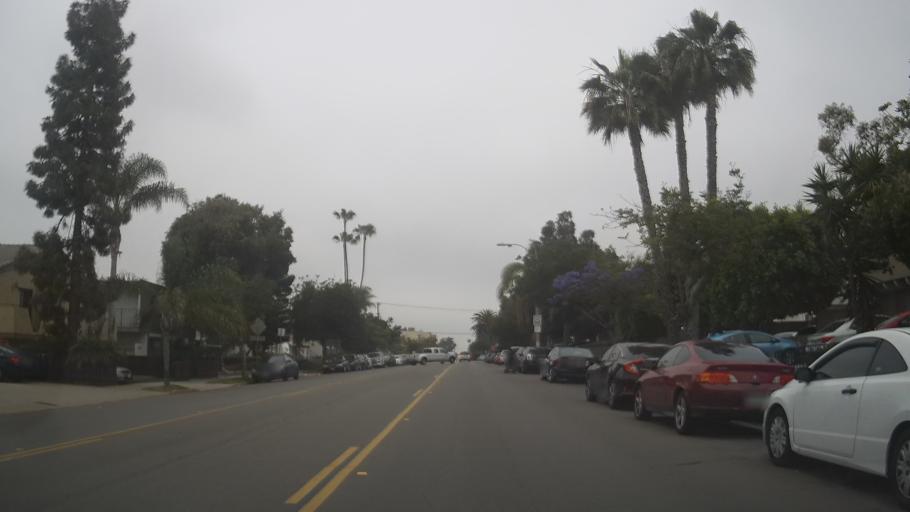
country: US
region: California
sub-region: San Diego County
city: San Diego
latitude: 32.7507
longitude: -117.1388
